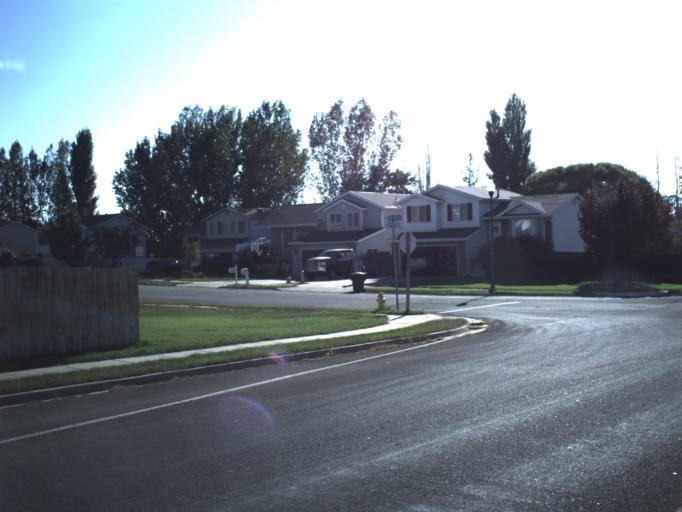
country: US
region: Utah
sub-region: Davis County
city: Clinton
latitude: 41.1399
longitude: -112.0412
